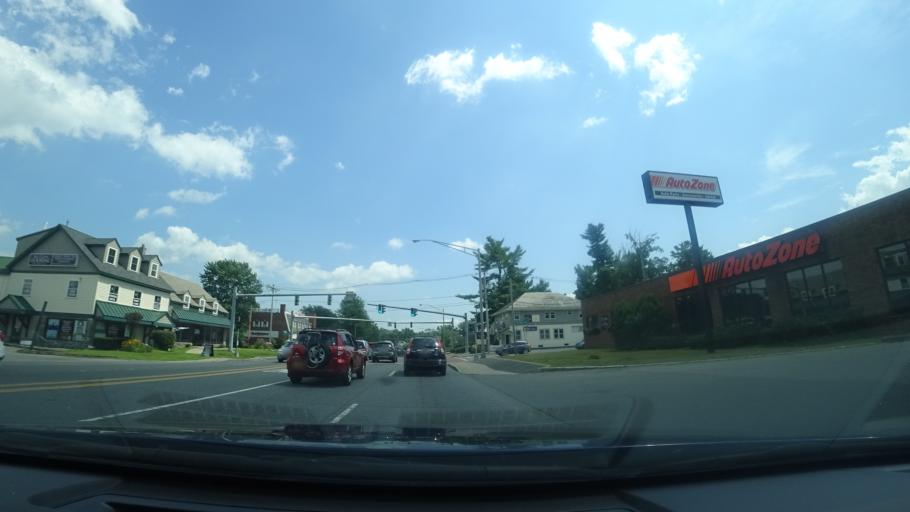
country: US
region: New York
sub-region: Warren County
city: Glens Falls North
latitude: 43.3274
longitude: -73.6675
